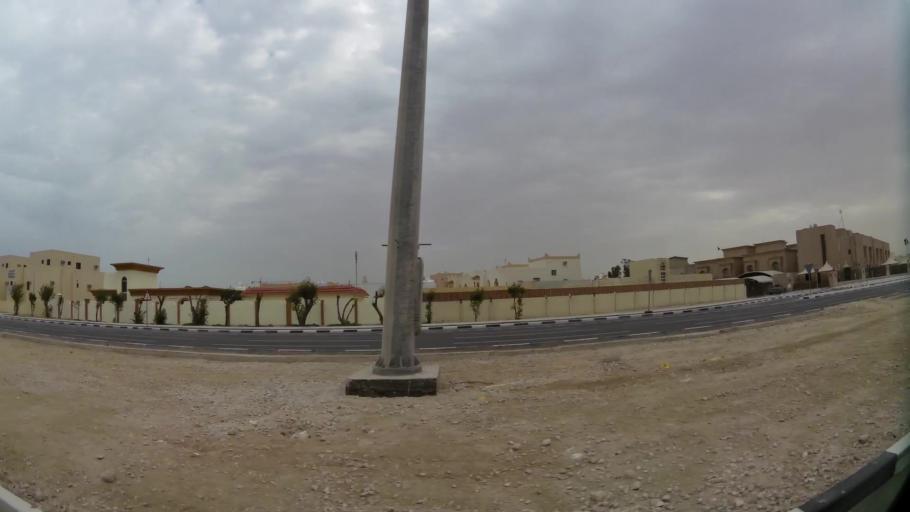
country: QA
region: Baladiyat ar Rayyan
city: Ar Rayyan
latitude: 25.3493
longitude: 51.4748
